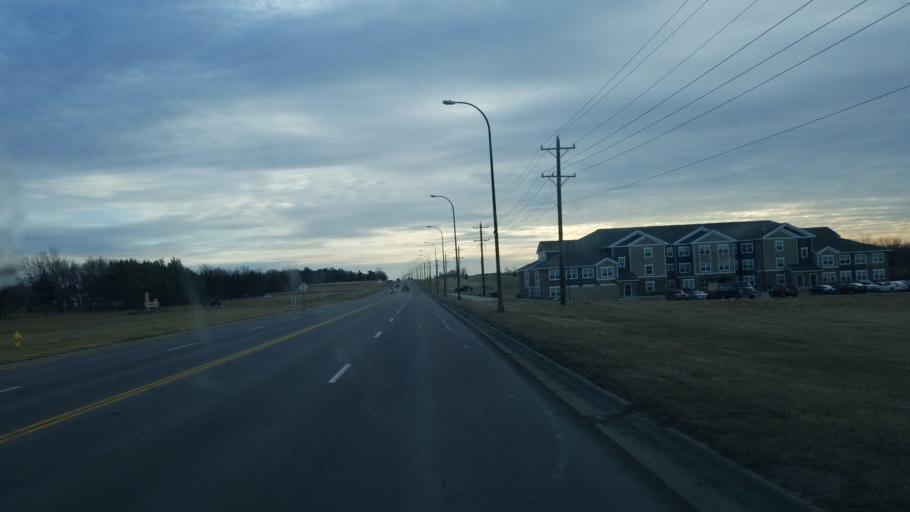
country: US
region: South Dakota
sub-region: Yankton County
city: Yankton
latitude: 42.9088
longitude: -97.4155
